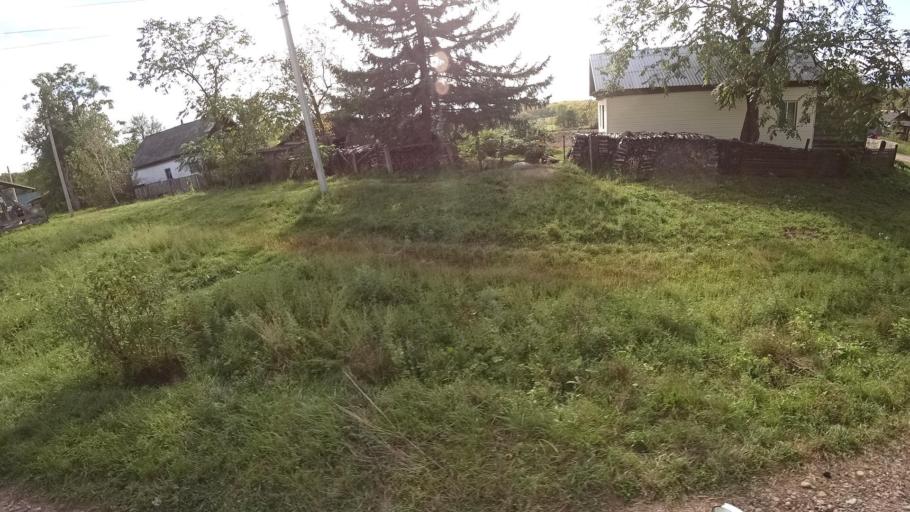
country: RU
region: Primorskiy
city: Dostoyevka
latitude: 44.2934
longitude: 133.4486
